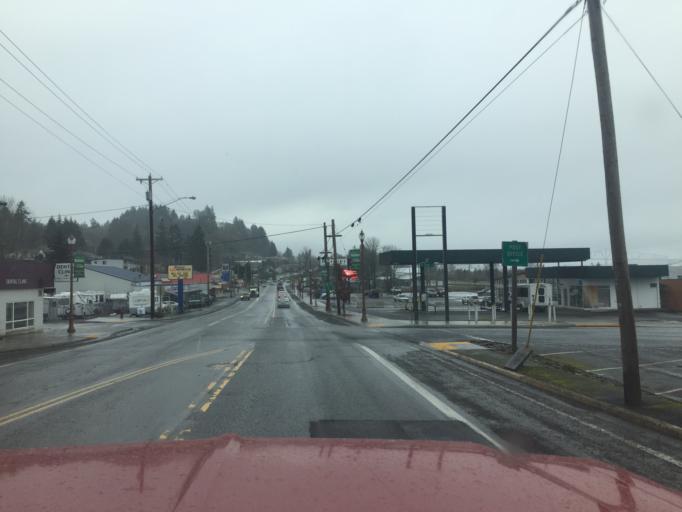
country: US
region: Oregon
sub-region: Columbia County
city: Rainier
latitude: 46.0893
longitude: -122.9366
